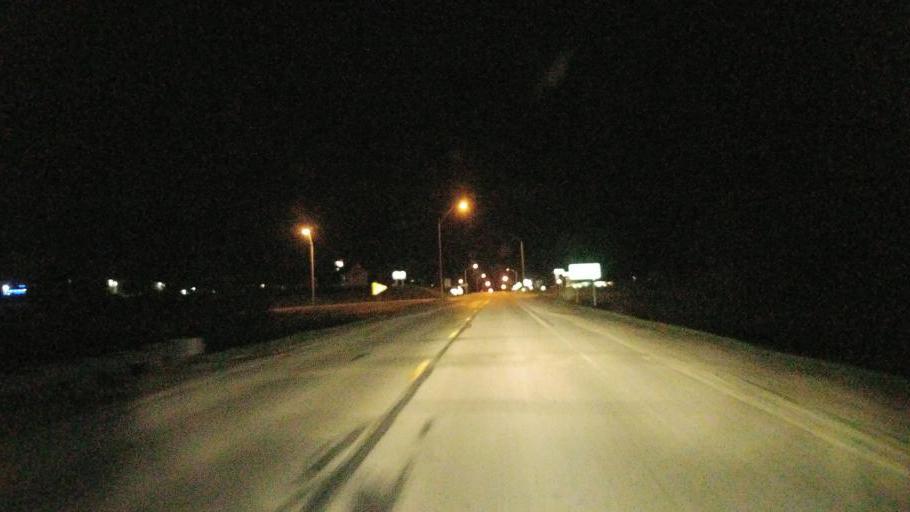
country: US
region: Iowa
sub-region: Decatur County
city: Lamoni
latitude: 40.6237
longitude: -93.8913
